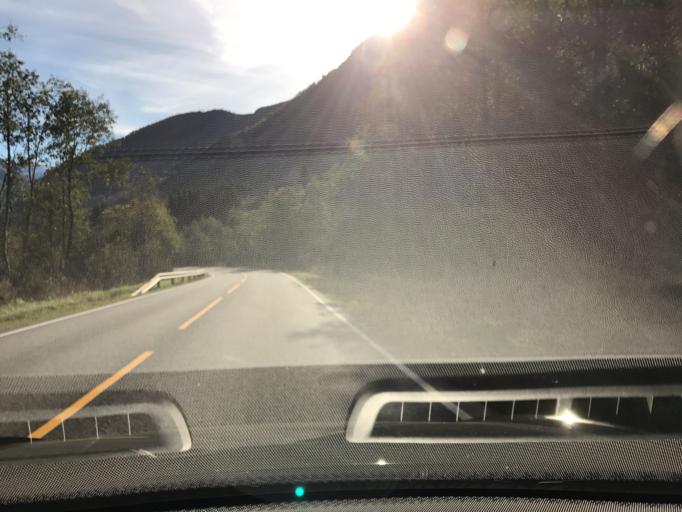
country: NO
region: Sogn og Fjordane
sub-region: Leikanger
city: Hermansverk
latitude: 61.4509
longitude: 6.7414
